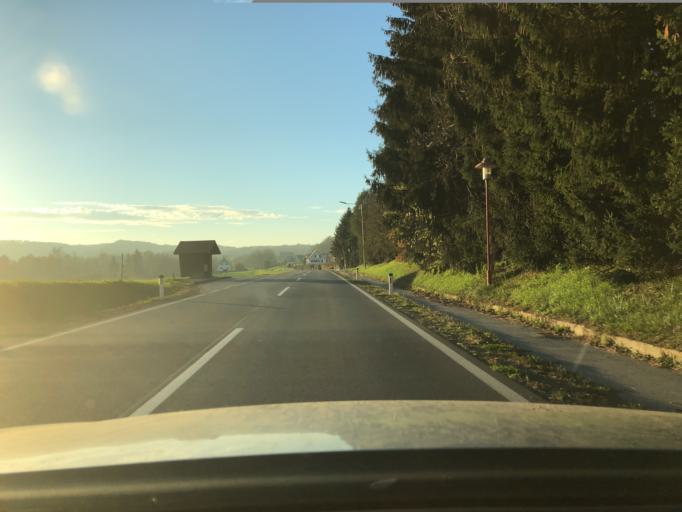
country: AT
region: Styria
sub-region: Politischer Bezirk Weiz
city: Sinabelkirchen
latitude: 47.1015
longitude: 15.8052
